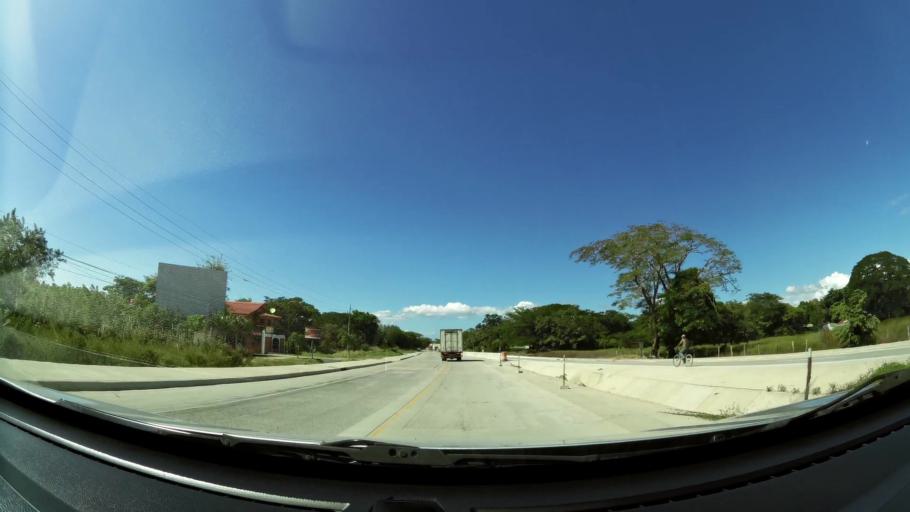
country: CR
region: Guanacaste
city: Liberia
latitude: 10.5765
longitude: -85.4023
